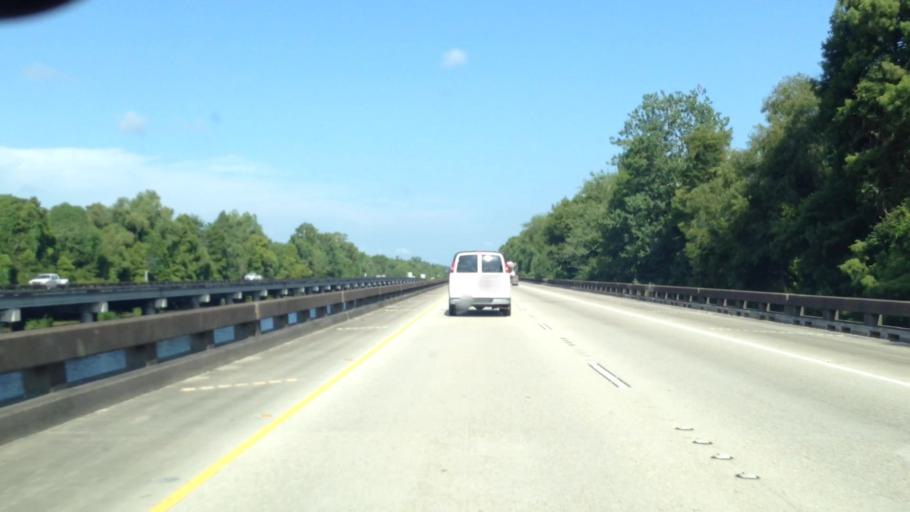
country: US
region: Louisiana
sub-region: Saint John the Baptist Parish
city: Reserve
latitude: 30.1123
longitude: -90.5564
